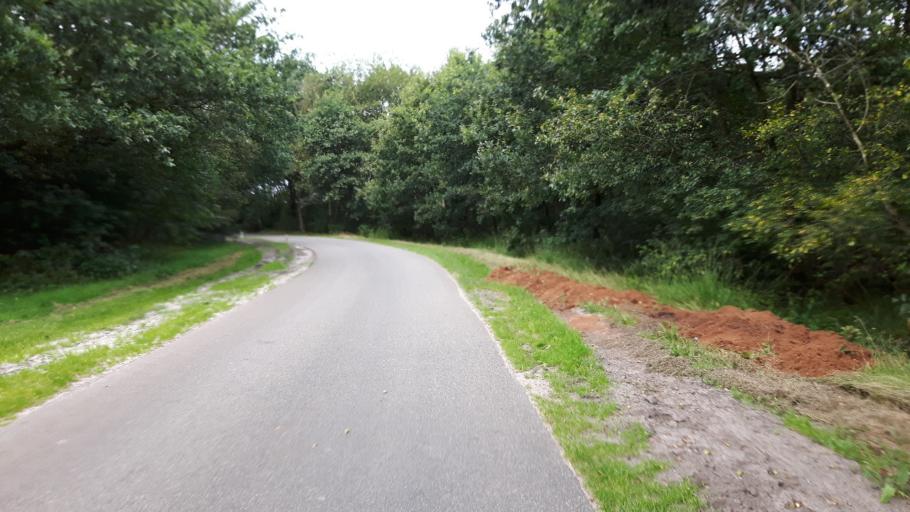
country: NL
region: Groningen
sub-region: Gemeente Leek
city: Leek
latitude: 53.1055
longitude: 6.3893
